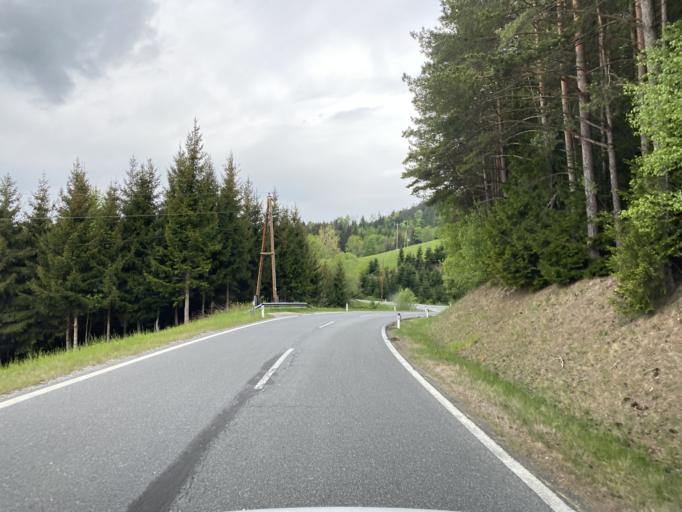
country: AT
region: Styria
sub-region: Politischer Bezirk Weiz
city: Gschaid bei Birkfeld
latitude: 47.3432
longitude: 15.7427
